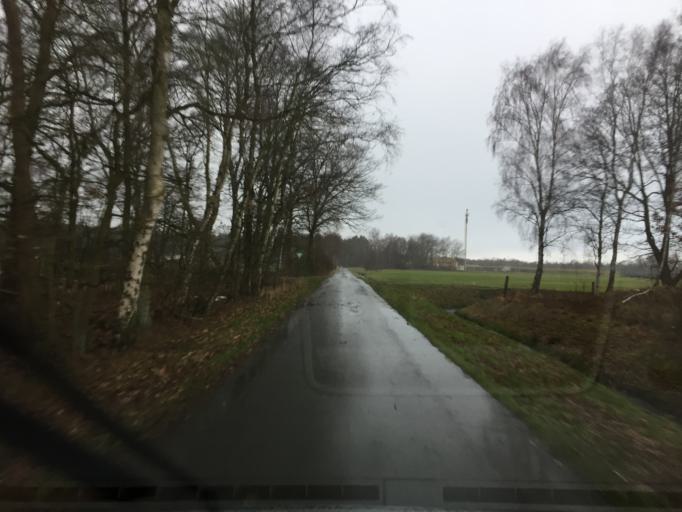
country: DE
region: Lower Saxony
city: Maasen
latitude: 52.6508
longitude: 8.8734
